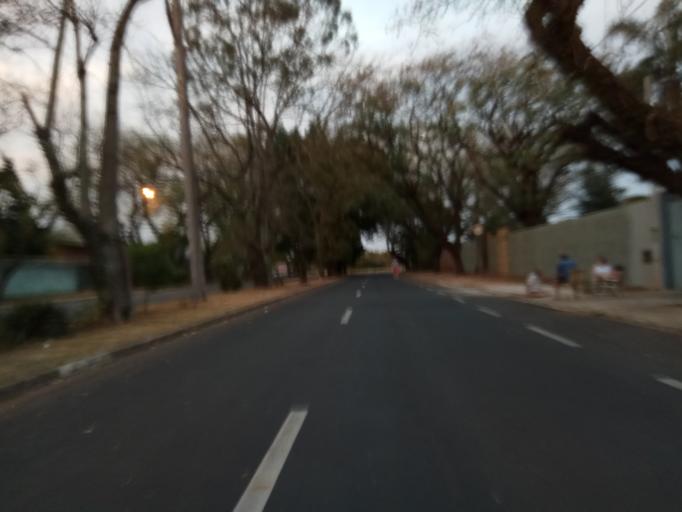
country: BR
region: Sao Paulo
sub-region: Piracicaba
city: Piracicaba
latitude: -22.7529
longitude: -47.5858
